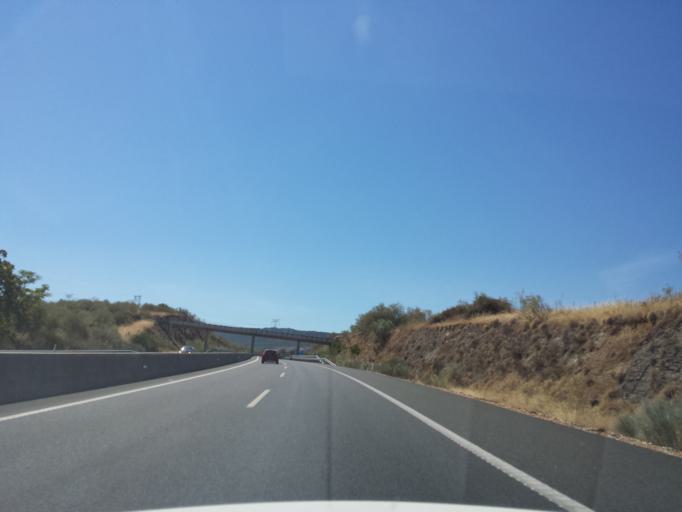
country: ES
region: Extremadura
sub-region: Provincia de Caceres
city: Casas de Miravete
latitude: 39.7453
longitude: -5.7263
